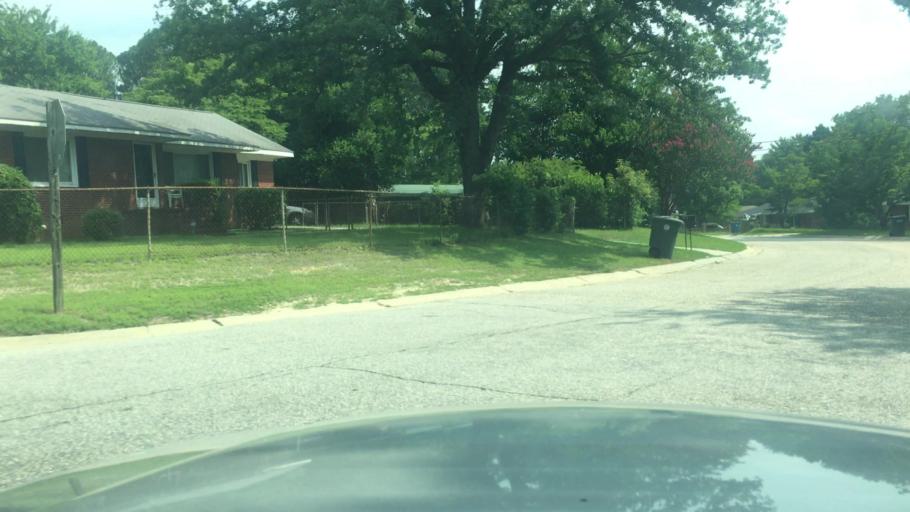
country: US
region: North Carolina
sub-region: Cumberland County
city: Hope Mills
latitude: 35.0296
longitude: -78.9452
